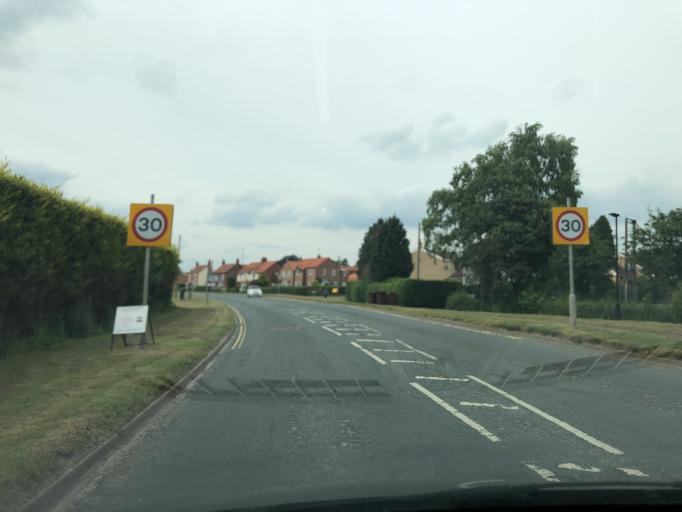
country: GB
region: England
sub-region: North Yorkshire
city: Great Habton
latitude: 54.2653
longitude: -0.9237
